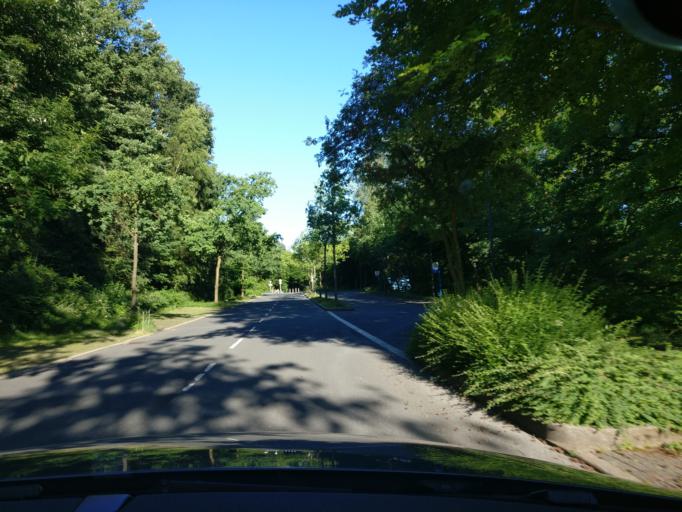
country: DE
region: North Rhine-Westphalia
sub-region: Regierungsbezirk Dusseldorf
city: Wuppertal
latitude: 51.2409
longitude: 7.1507
